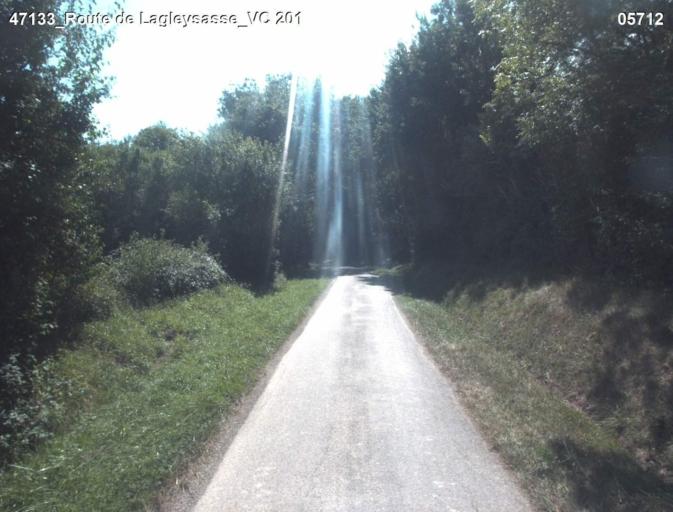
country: FR
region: Aquitaine
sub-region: Departement du Lot-et-Garonne
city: Laplume
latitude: 44.0664
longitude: 0.4949
